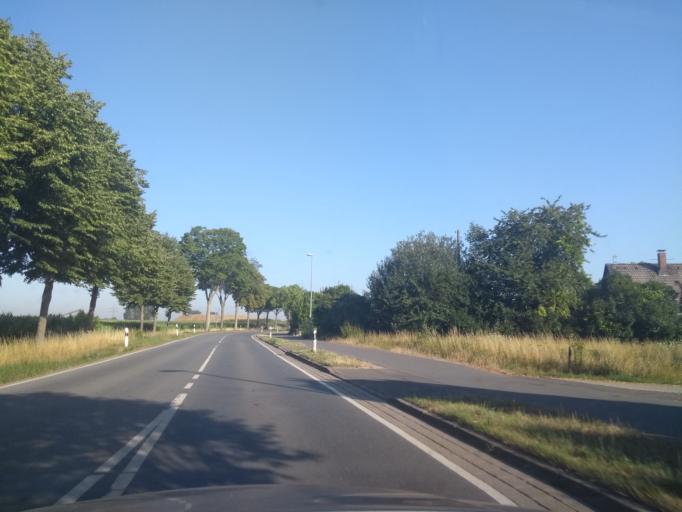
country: DE
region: North Rhine-Westphalia
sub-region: Regierungsbezirk Dusseldorf
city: Kleve
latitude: 51.8156
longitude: 6.1206
